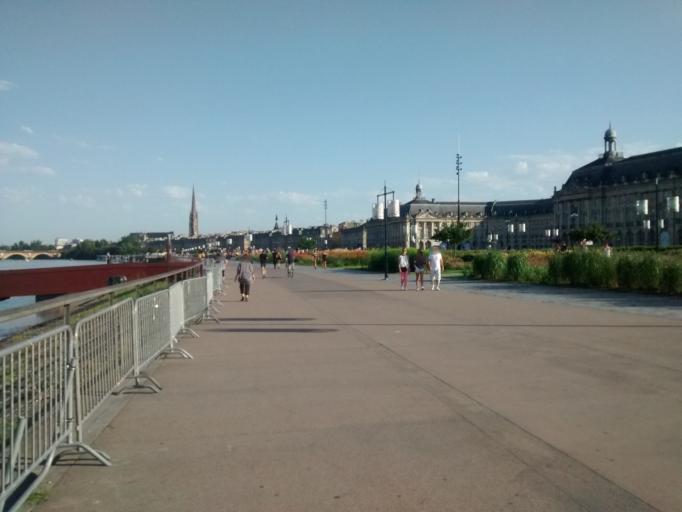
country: FR
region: Aquitaine
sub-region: Departement de la Gironde
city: Bordeaux
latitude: 44.8436
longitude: -0.5689
